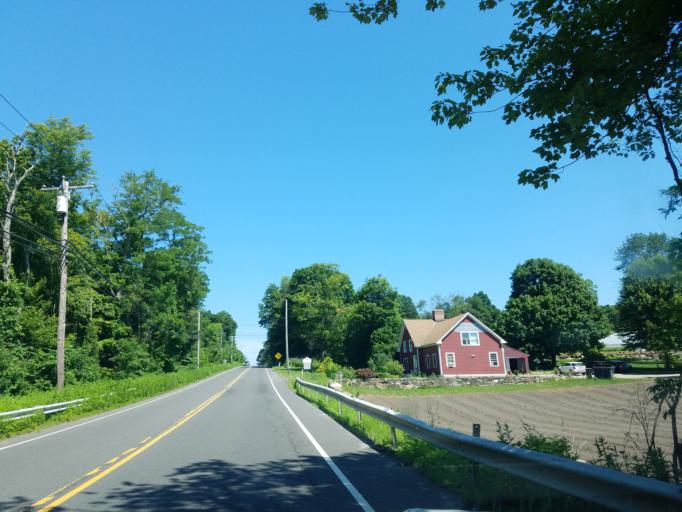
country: US
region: Connecticut
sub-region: Fairfield County
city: Trumbull
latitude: 41.2568
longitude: -73.2850
